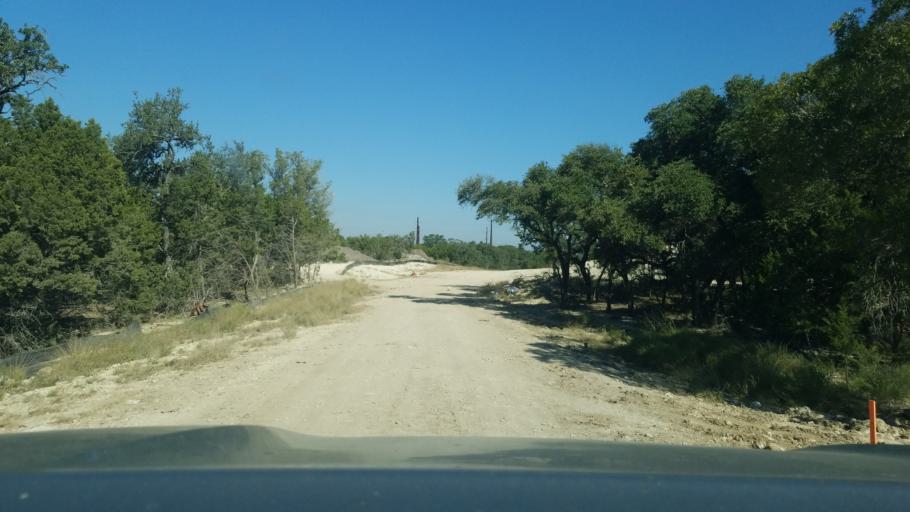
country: US
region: Texas
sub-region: Kendall County
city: Boerne
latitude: 29.7576
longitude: -98.7194
